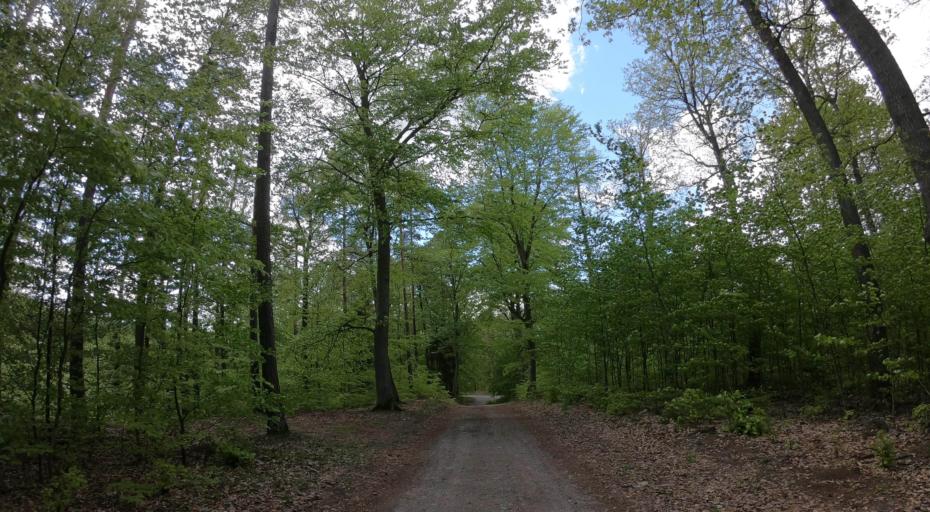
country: PL
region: West Pomeranian Voivodeship
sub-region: Powiat lobeski
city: Lobez
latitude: 53.5973
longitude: 15.6173
